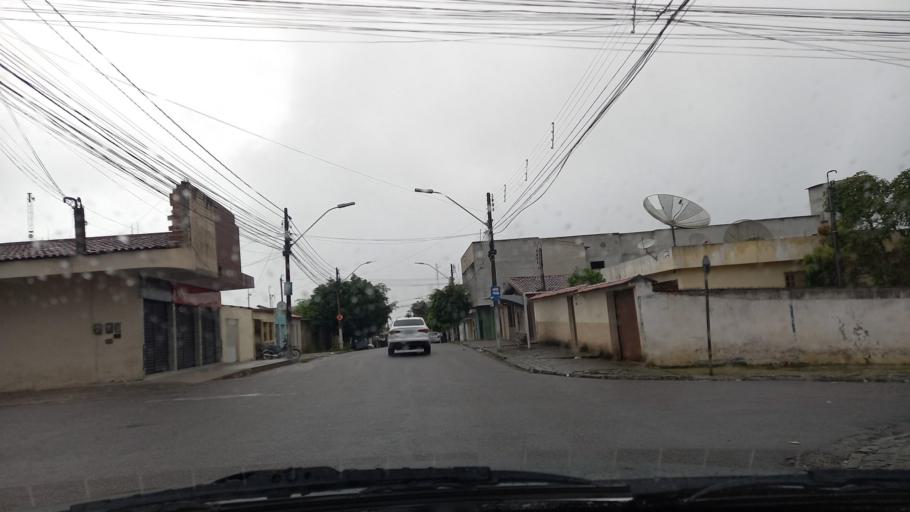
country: BR
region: Pernambuco
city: Garanhuns
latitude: -8.8823
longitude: -36.4980
